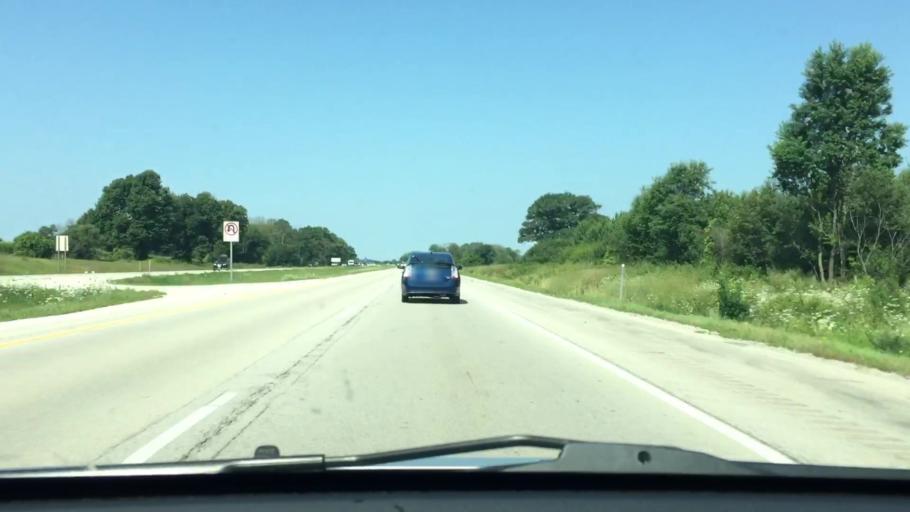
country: US
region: Wisconsin
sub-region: Waukesha County
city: Oconomowoc
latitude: 43.0706
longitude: -88.5431
